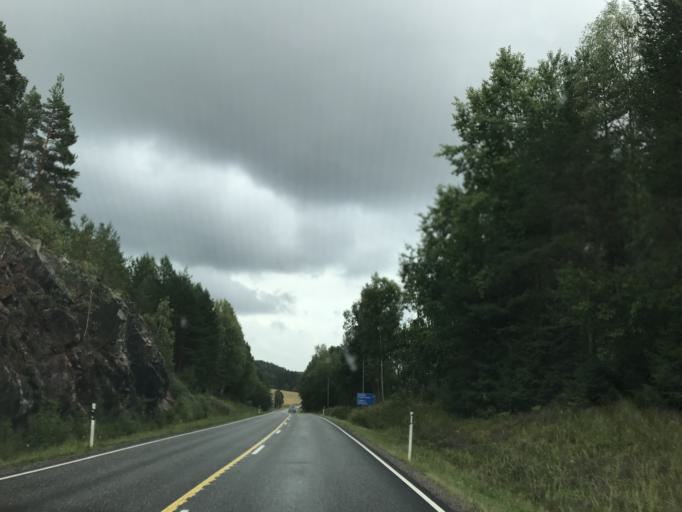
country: FI
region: Varsinais-Suomi
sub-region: Salo
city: Pernioe
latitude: 60.0929
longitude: 23.2232
